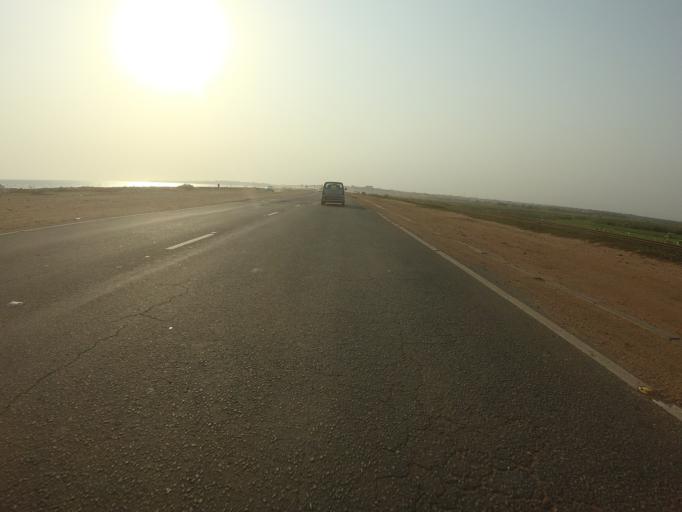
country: GH
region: Greater Accra
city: Nungua
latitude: 5.6137
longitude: -0.0321
